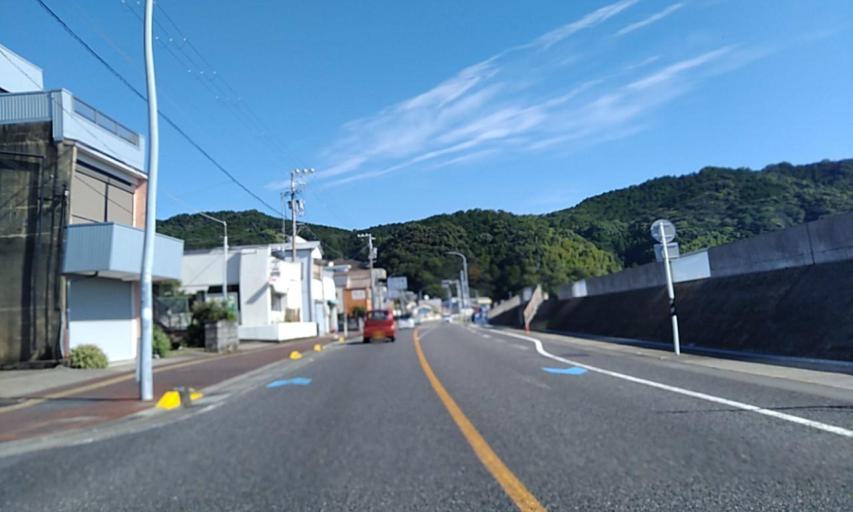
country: JP
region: Wakayama
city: Shingu
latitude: 33.8901
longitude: 136.1047
